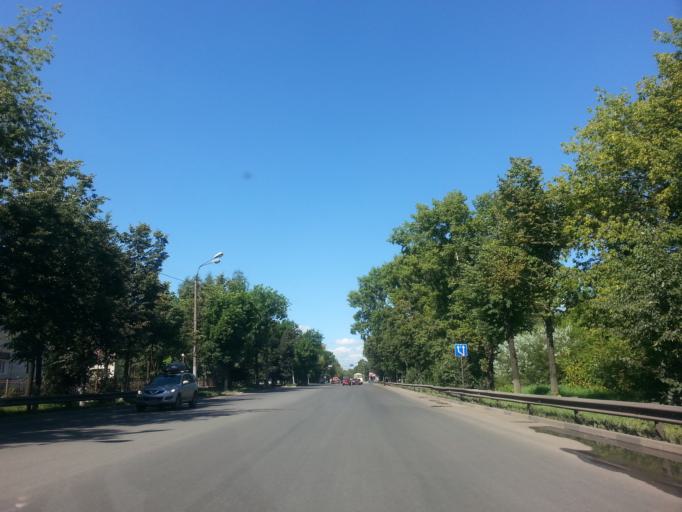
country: RU
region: Nizjnij Novgorod
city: Gorbatovka
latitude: 56.3429
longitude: 43.8419
